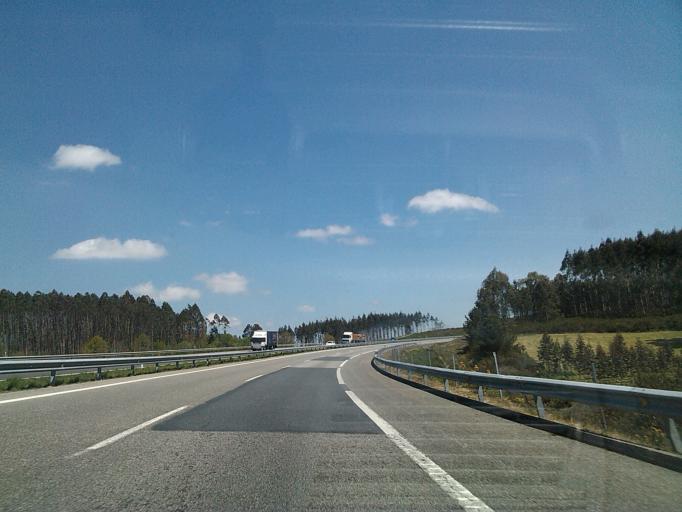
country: ES
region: Galicia
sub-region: Provincia da Coruna
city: Oroso
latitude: 42.9097
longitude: -8.4609
